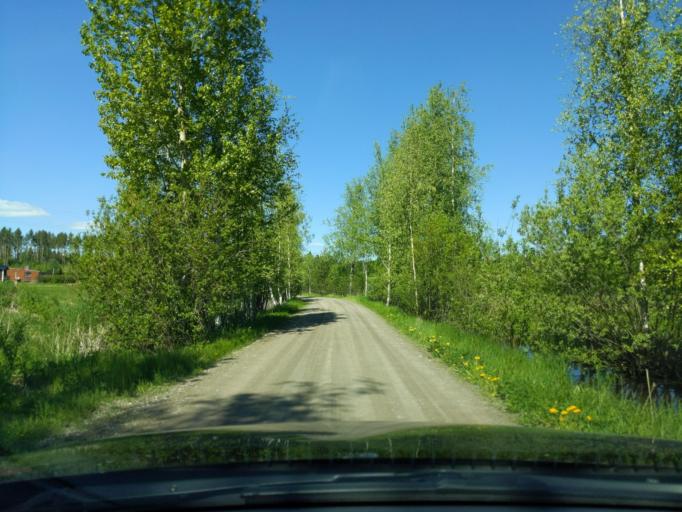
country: FI
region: Paijanne Tavastia
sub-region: Lahti
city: Lahti
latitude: 61.0565
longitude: 25.6816
